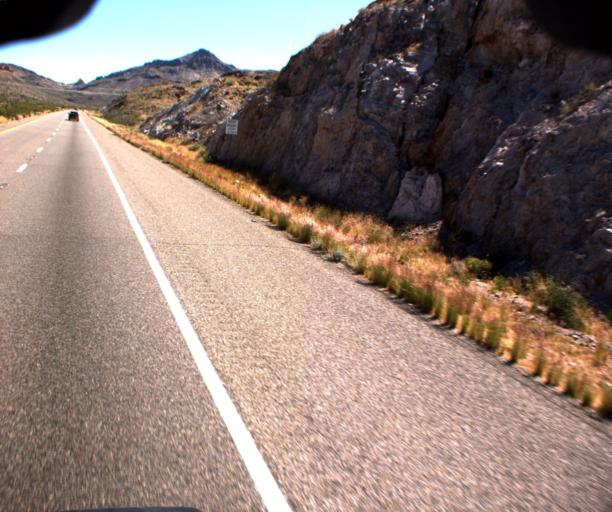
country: US
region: Nevada
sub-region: Clark County
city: Laughlin
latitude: 35.1968
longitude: -114.4299
